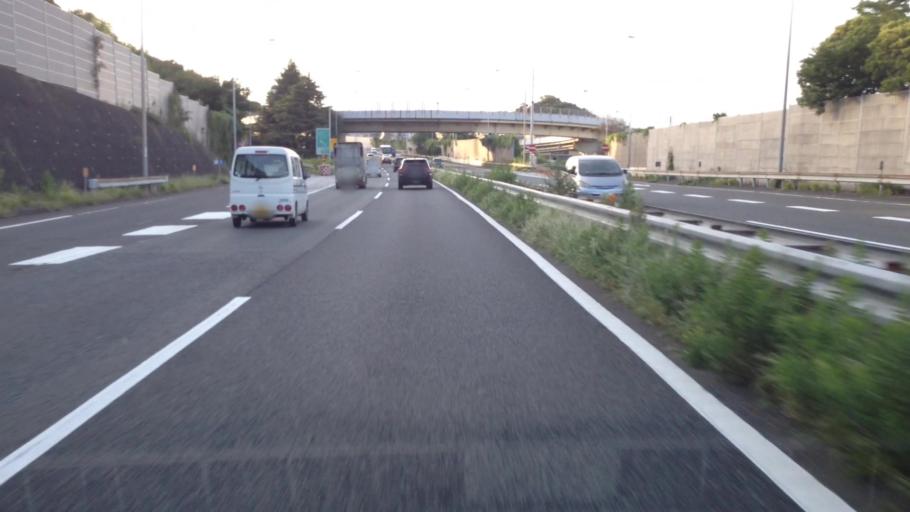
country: JP
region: Kanagawa
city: Kamakura
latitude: 35.3812
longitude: 139.5854
